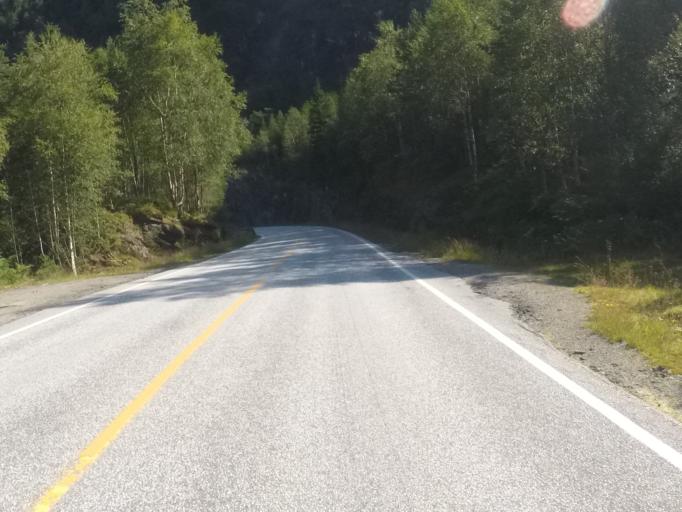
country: NO
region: Sogn og Fjordane
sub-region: Bremanger
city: Svelgen
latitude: 61.6185
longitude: 5.3135
